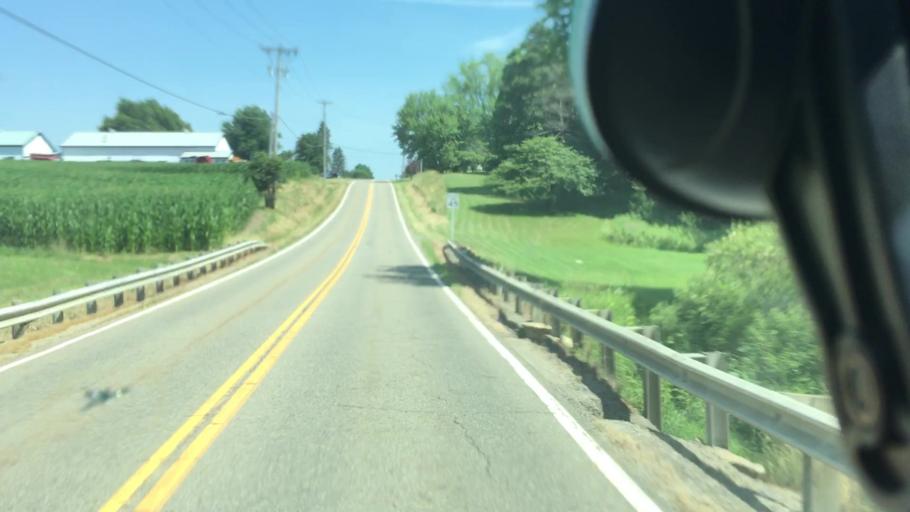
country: US
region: Ohio
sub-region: Columbiana County
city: Salem
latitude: 40.8298
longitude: -80.8580
